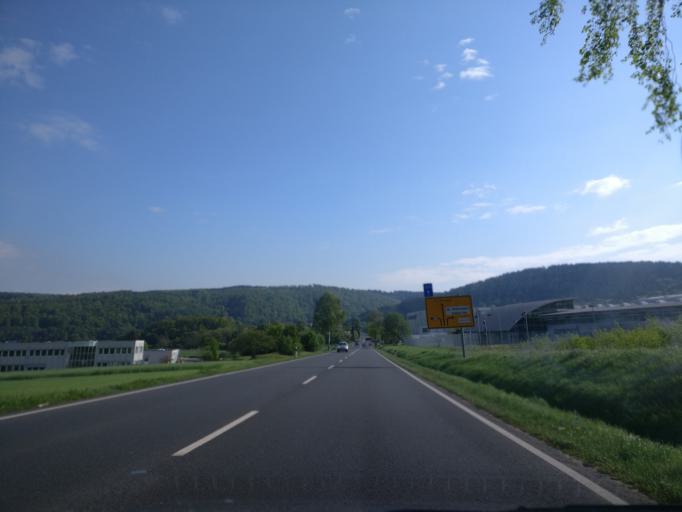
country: DE
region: Lower Saxony
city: Hannoversch Munden
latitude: 51.4357
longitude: 9.6542
